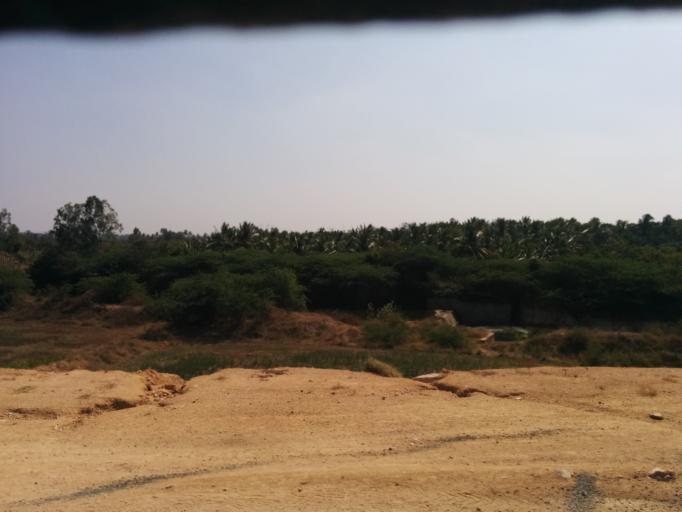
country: IN
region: Karnataka
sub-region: Gadag
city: Gadag
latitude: 15.4374
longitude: 75.5422
